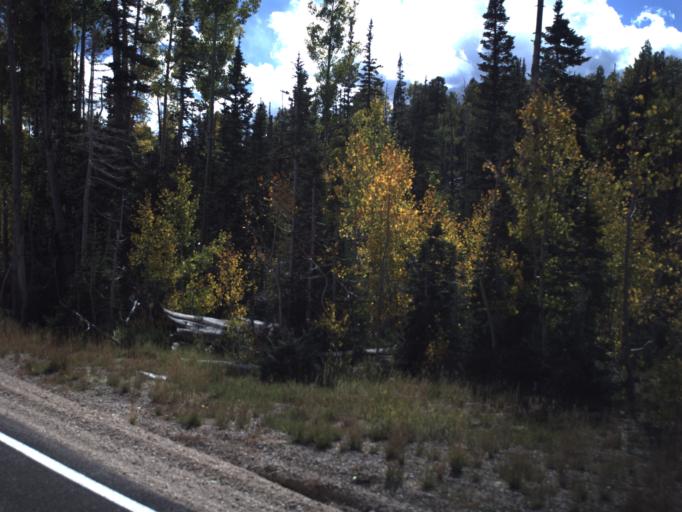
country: US
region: Utah
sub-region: Iron County
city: Parowan
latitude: 37.5505
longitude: -112.7866
